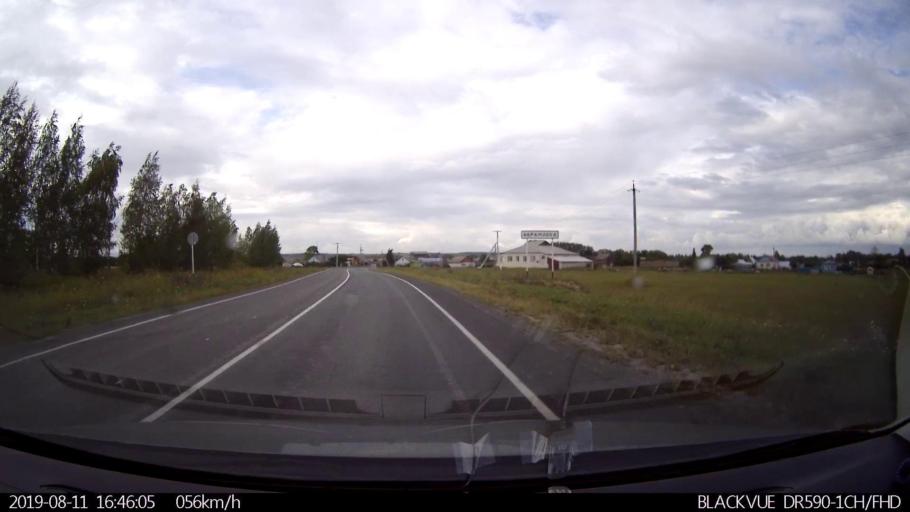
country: RU
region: Ulyanovsk
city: Mayna
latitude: 54.1956
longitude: 47.6877
